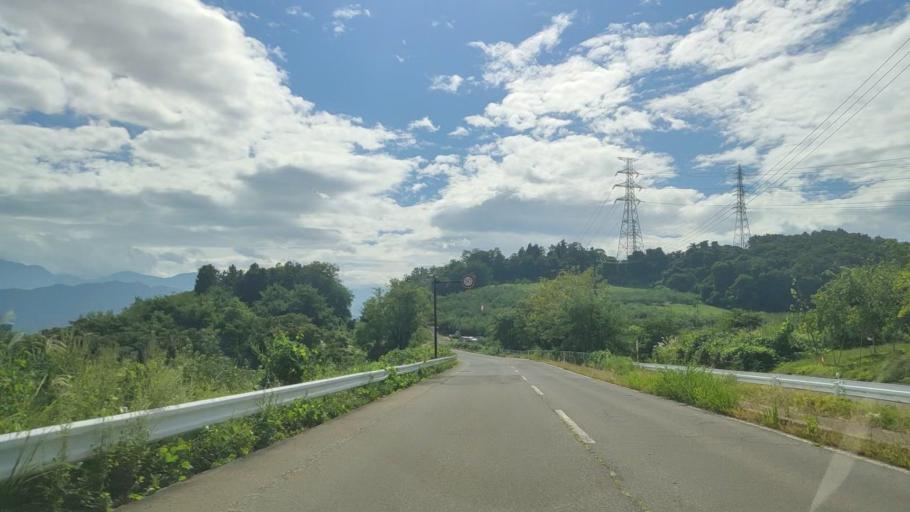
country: JP
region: Nagano
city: Nakano
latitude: 36.7370
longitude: 138.3050
